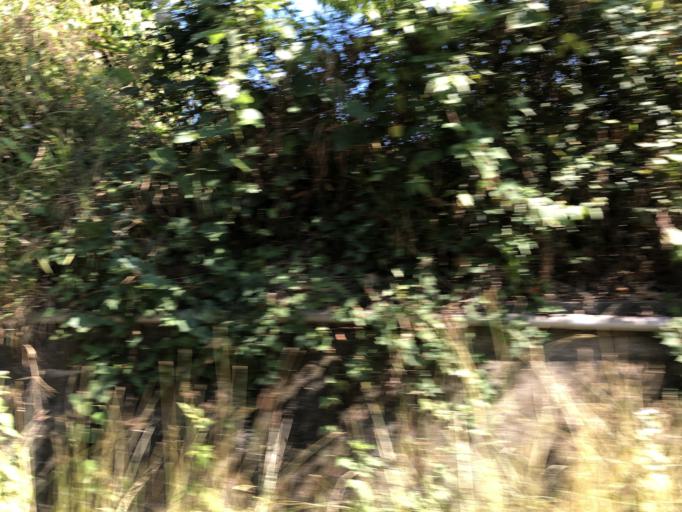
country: TW
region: Taiwan
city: Yujing
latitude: 23.0572
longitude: 120.3788
